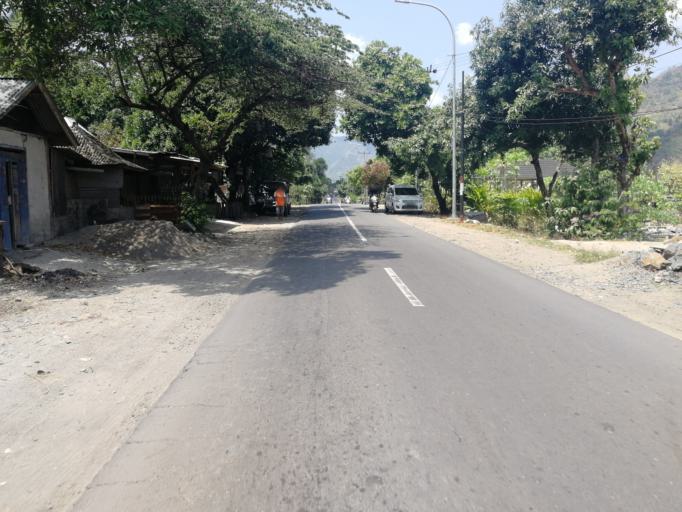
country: ID
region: West Nusa Tenggara
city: Karangsubagan
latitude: -8.4230
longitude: 116.0931
